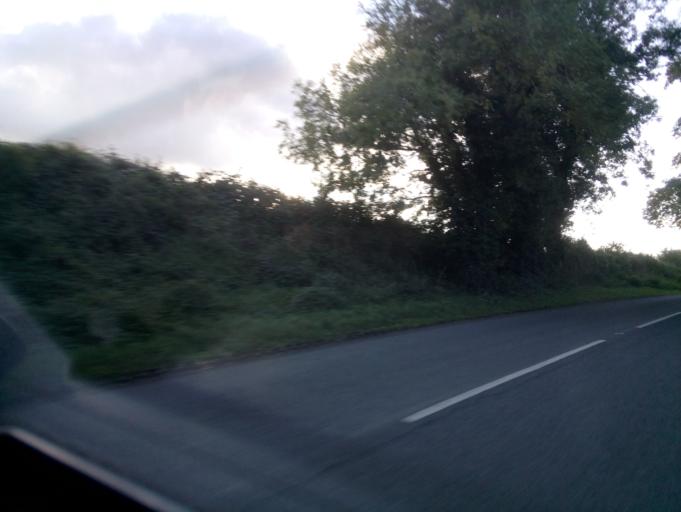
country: GB
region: England
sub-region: Worcestershire
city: Great Malvern
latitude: 52.0137
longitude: -2.3112
